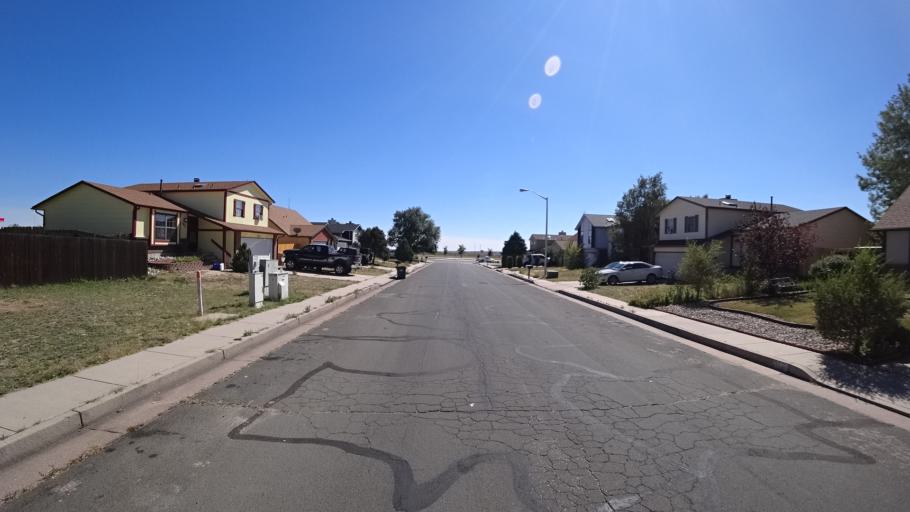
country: US
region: Colorado
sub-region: El Paso County
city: Stratmoor
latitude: 38.7826
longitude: -104.7411
